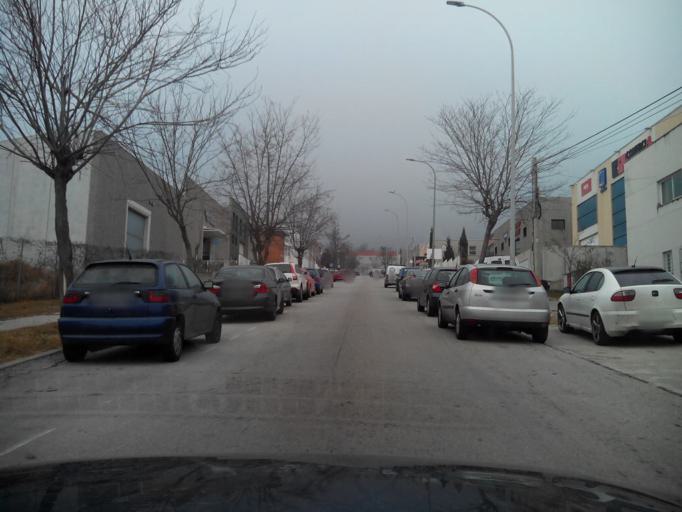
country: ES
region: Catalonia
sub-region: Provincia de Barcelona
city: Berga
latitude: 42.0949
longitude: 1.8256
